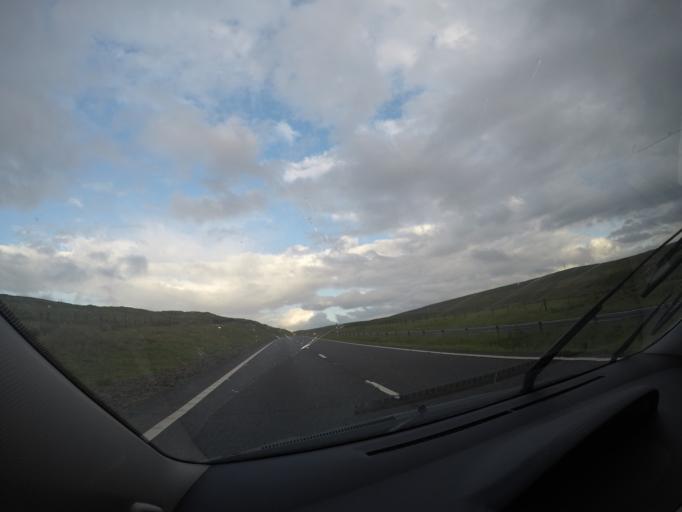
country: GB
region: England
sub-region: County Durham
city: Holwick
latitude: 54.5147
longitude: -2.2039
